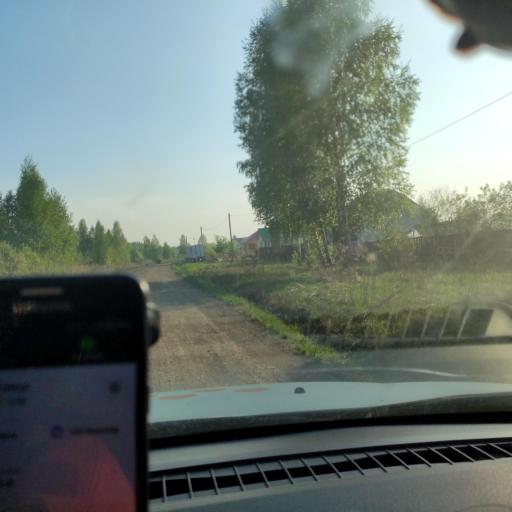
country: RU
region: Bashkortostan
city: Kabakovo
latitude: 54.7261
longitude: 56.2269
